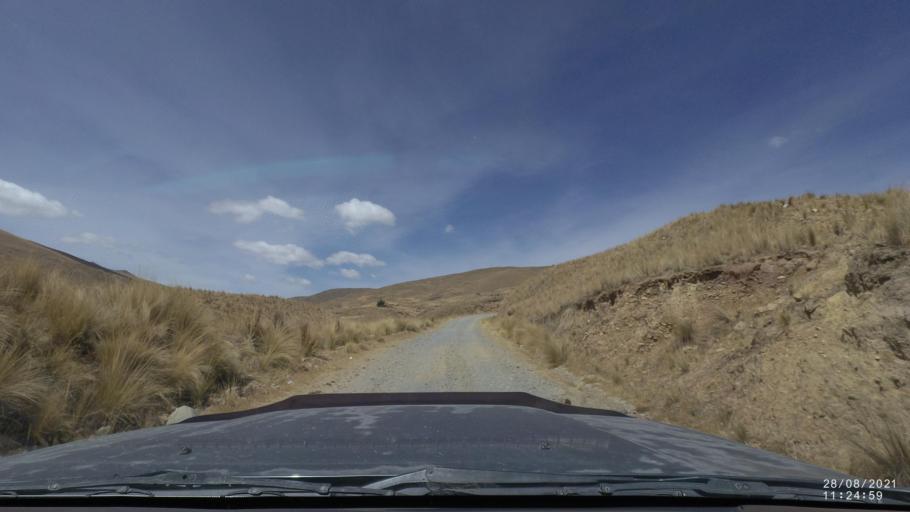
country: BO
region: Cochabamba
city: Sipe Sipe
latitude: -17.1700
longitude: -66.3525
